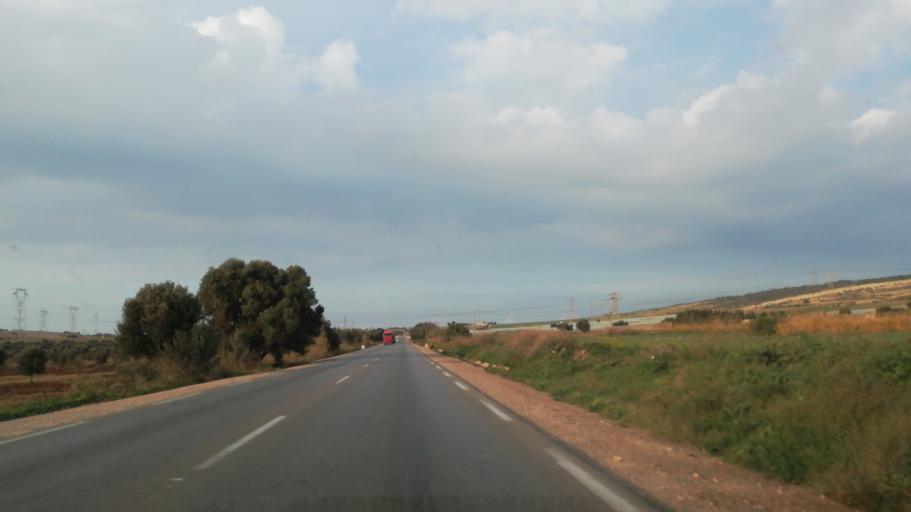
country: DZ
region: Oran
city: Ain el Bya
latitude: 35.7733
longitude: -0.0968
